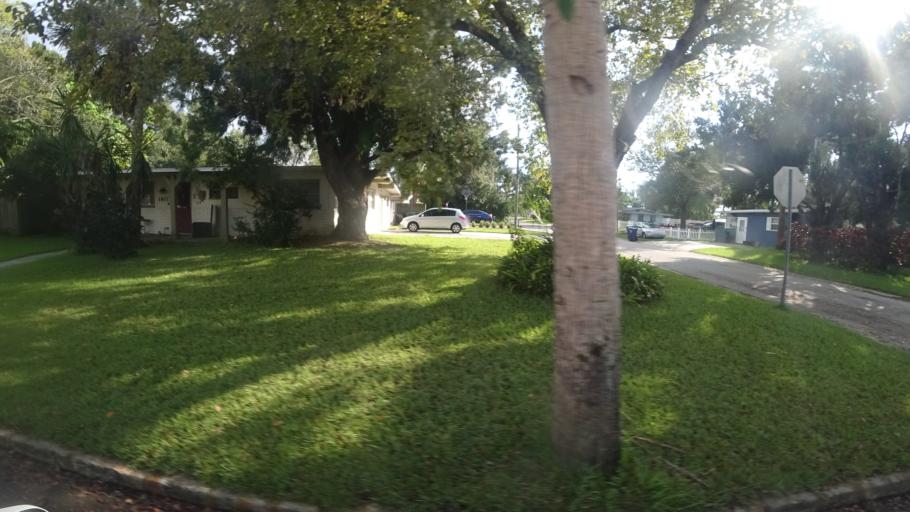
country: US
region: Florida
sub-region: Manatee County
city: Palmetto
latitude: 27.5176
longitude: -82.5880
